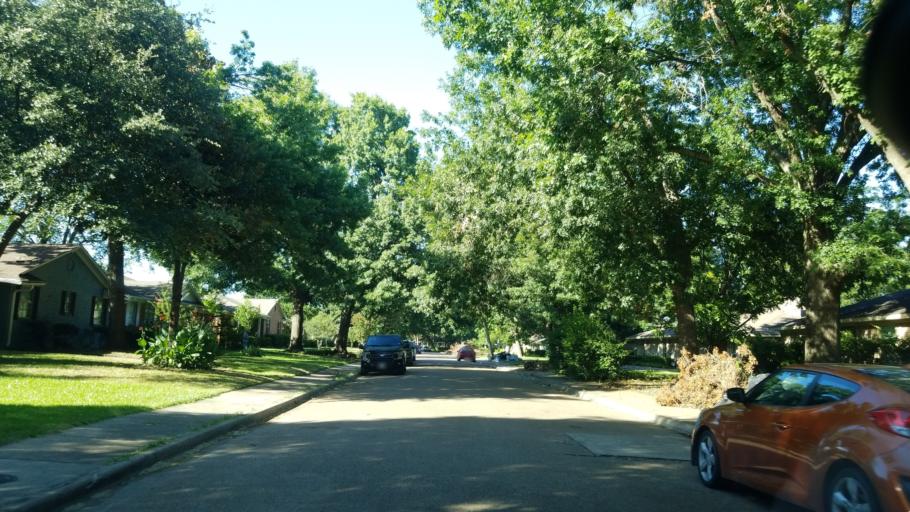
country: US
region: Texas
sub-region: Dallas County
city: Highland Park
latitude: 32.7880
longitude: -96.7073
